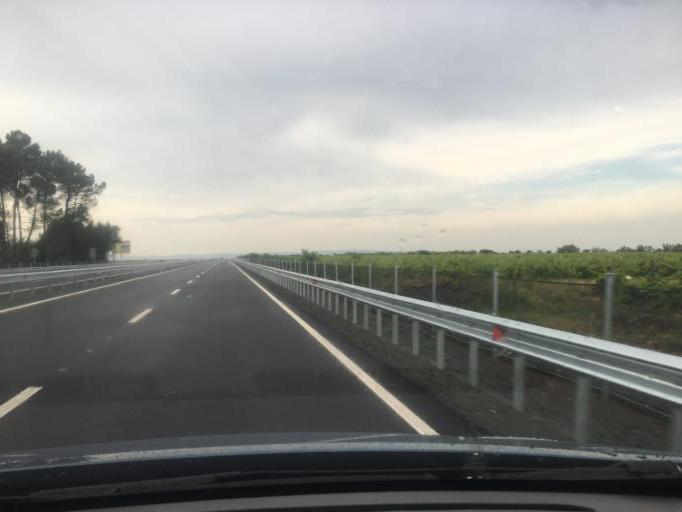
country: BG
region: Burgas
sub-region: Obshtina Pomorie
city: Pomorie
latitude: 42.5980
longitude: 27.6163
